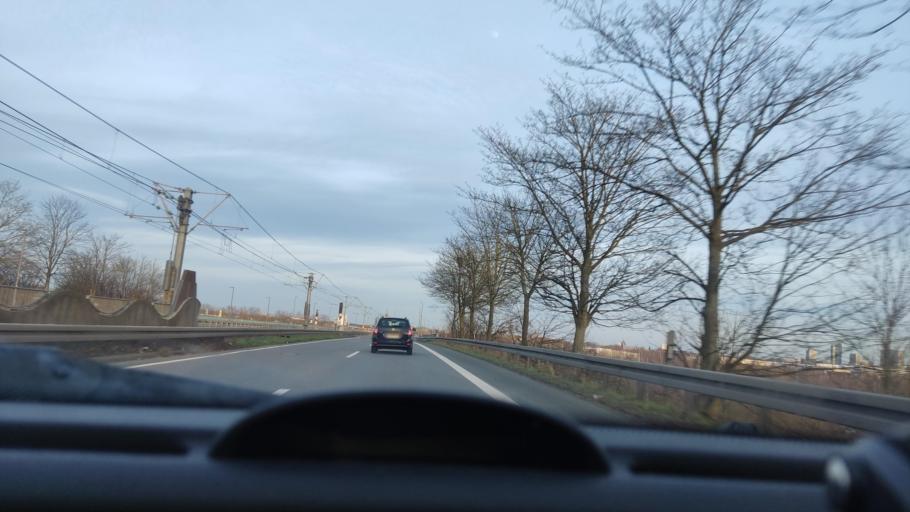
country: DE
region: North Rhine-Westphalia
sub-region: Regierungsbezirk Arnsberg
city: Dortmund
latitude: 51.5231
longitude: 7.4283
